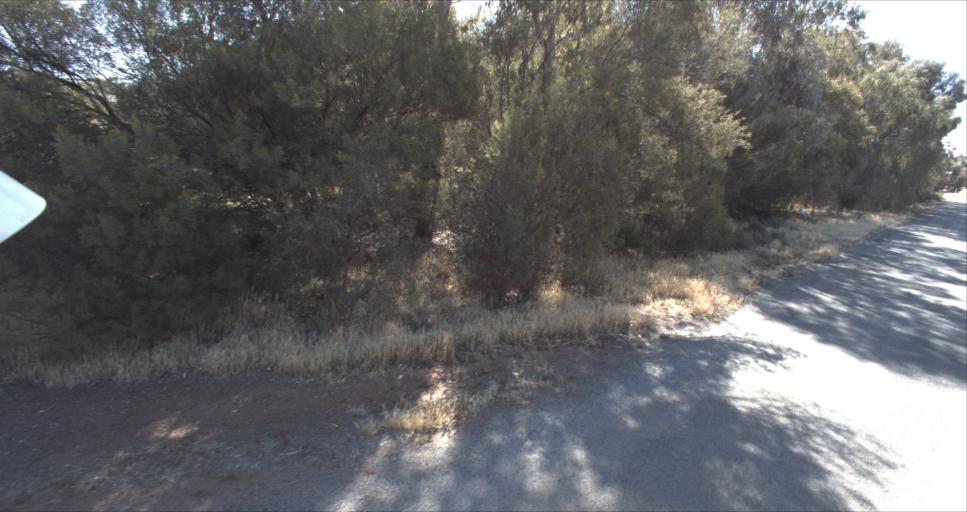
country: AU
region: New South Wales
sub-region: Leeton
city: Leeton
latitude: -34.5575
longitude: 146.3873
